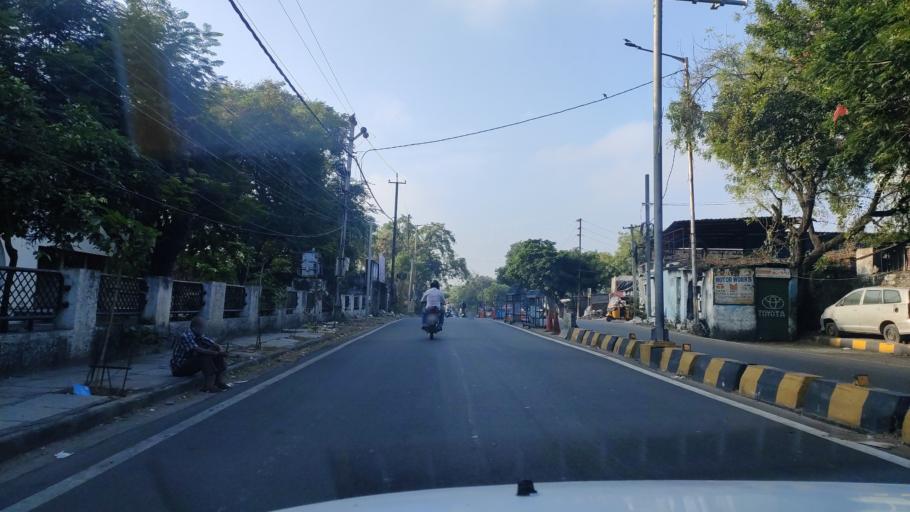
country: IN
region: Telangana
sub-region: Hyderabad
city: Hyderabad
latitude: 17.4215
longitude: 78.4852
